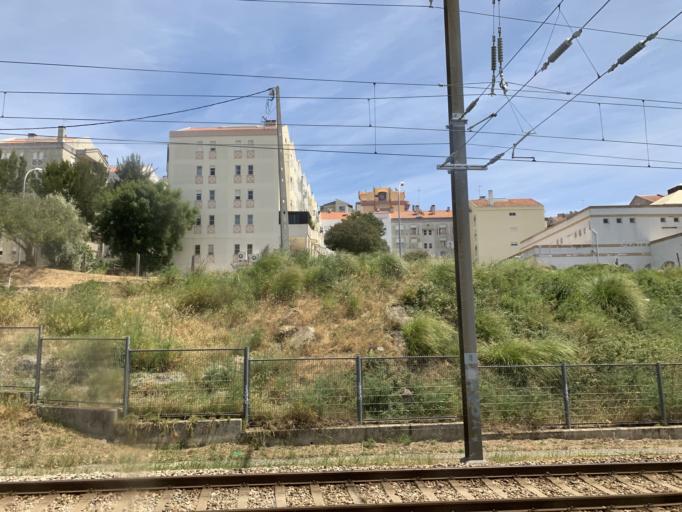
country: PT
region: Lisbon
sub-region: Sintra
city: Rio de Mouro
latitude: 38.7954
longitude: -9.3332
